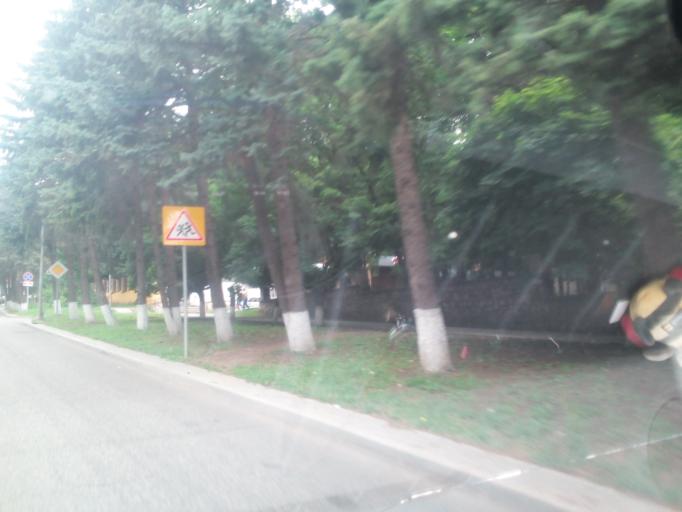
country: RU
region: Stavropol'skiy
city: Zheleznovodsk
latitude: 44.1337
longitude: 43.0470
